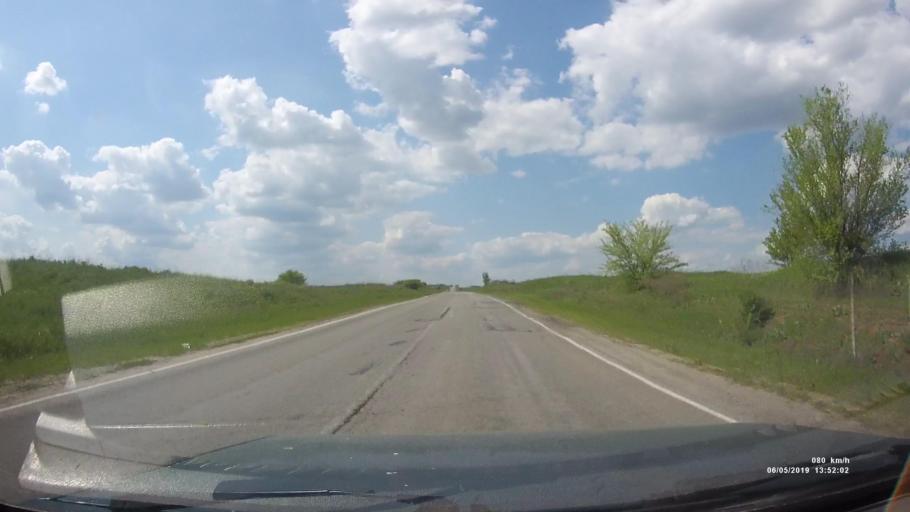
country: RU
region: Rostov
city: Melikhovskaya
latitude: 47.6597
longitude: 40.4830
